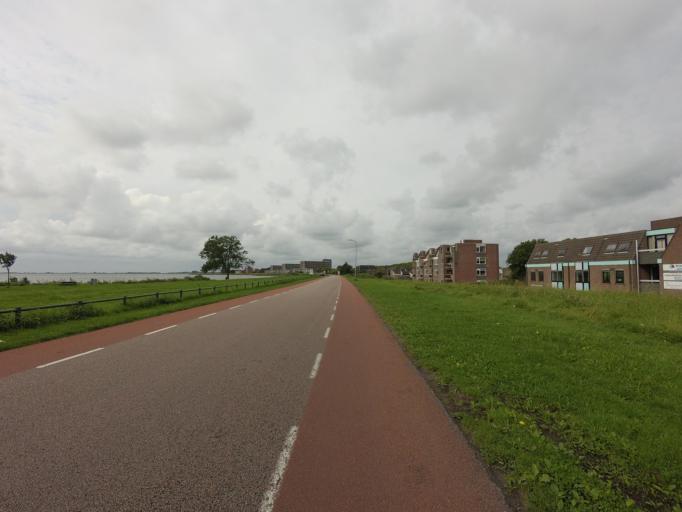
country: NL
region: North Holland
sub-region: Gemeente Hoorn
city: Hoorn
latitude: 52.6424
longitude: 5.0483
